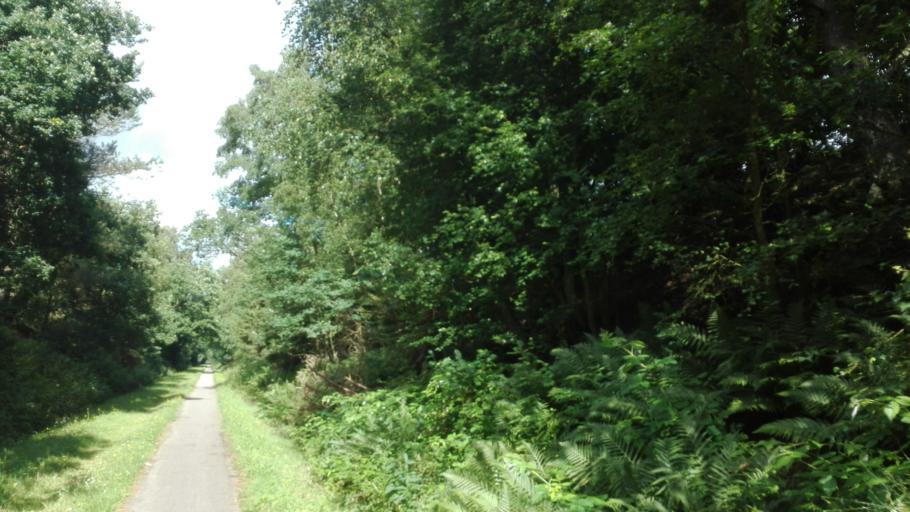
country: DK
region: Central Jutland
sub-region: Silkeborg Kommune
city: Virklund
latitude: 56.0632
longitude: 9.4832
